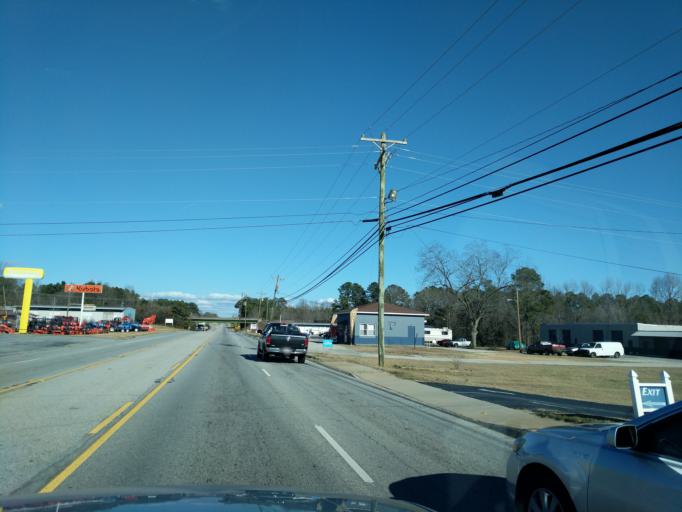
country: US
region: South Carolina
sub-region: Greenwood County
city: Greenwood
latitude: 34.2160
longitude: -82.1301
